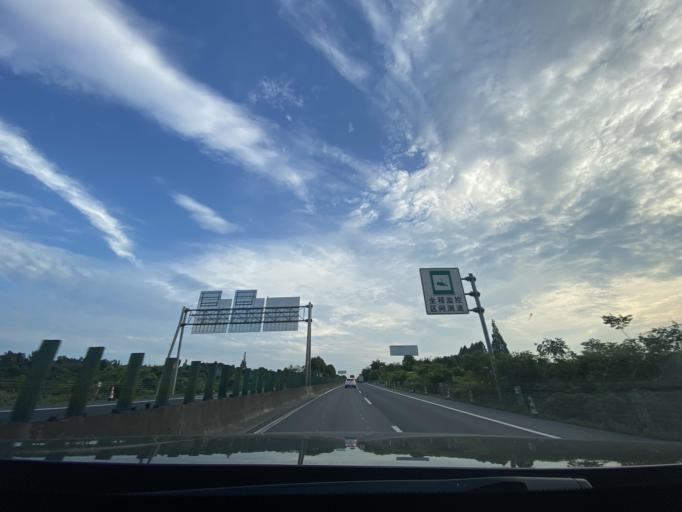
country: CN
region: Sichuan
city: Luojiang
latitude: 31.4102
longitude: 104.5788
